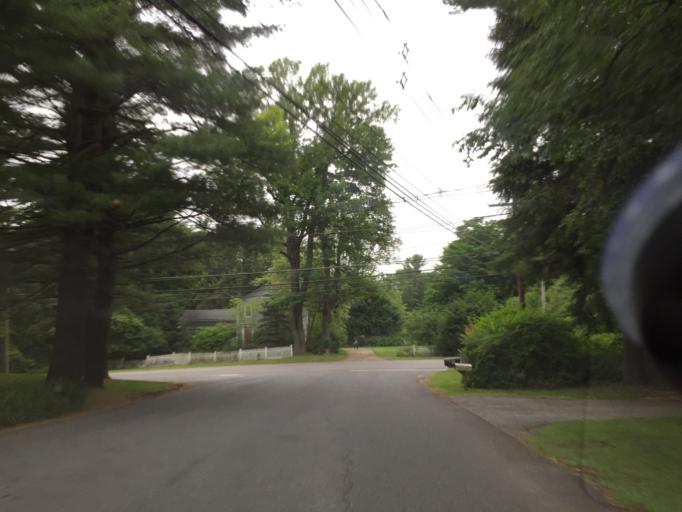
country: US
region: Connecticut
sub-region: Litchfield County
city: Litchfield
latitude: 41.8270
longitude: -73.2515
